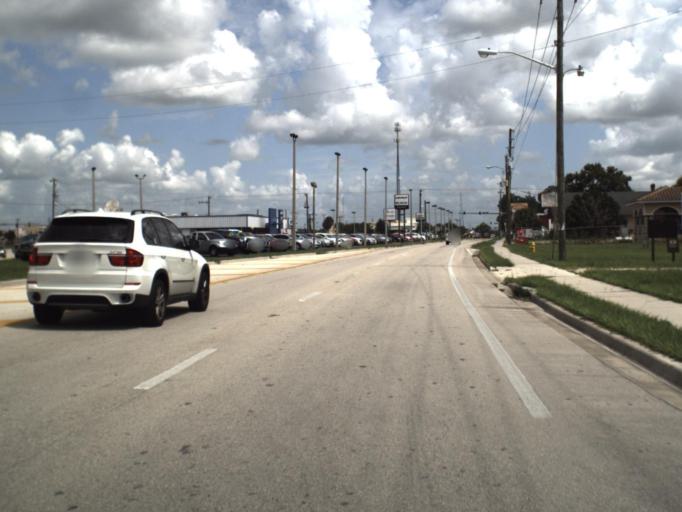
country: US
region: Florida
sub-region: DeSoto County
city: Arcadia
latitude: 27.2100
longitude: -81.8611
